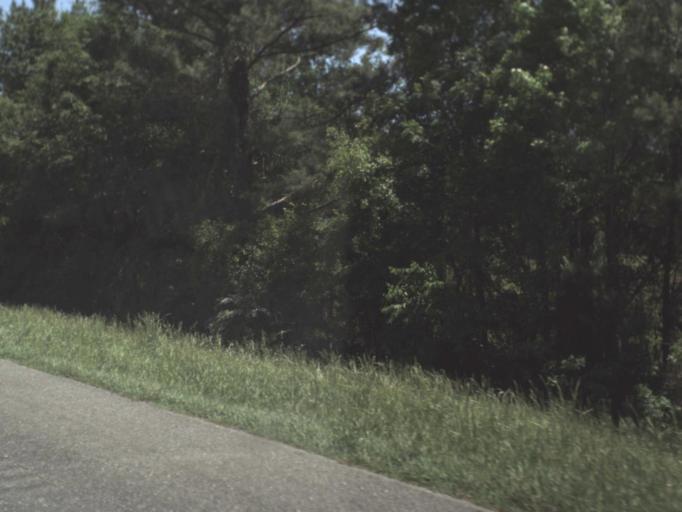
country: US
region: Florida
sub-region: Jefferson County
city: Monticello
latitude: 30.4784
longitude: -83.9242
